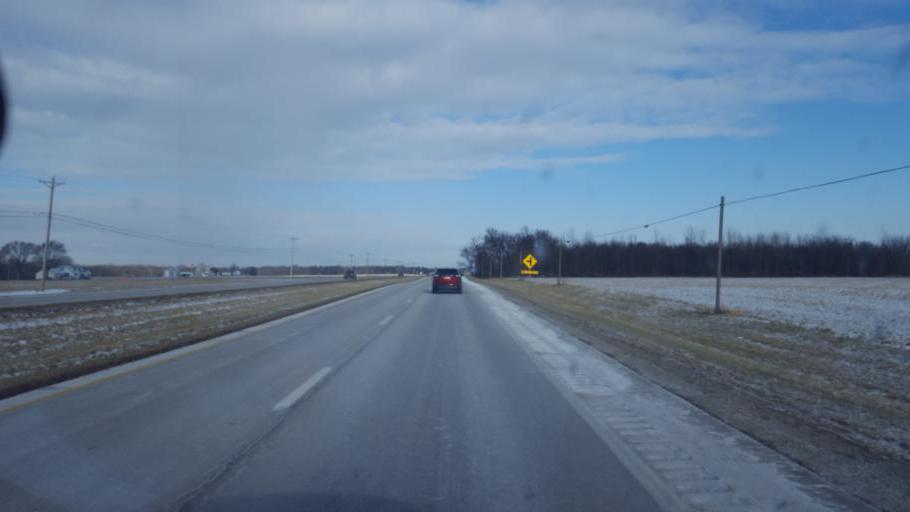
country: US
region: Ohio
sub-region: Pickaway County
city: Ashville
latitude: 39.6647
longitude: -82.9627
